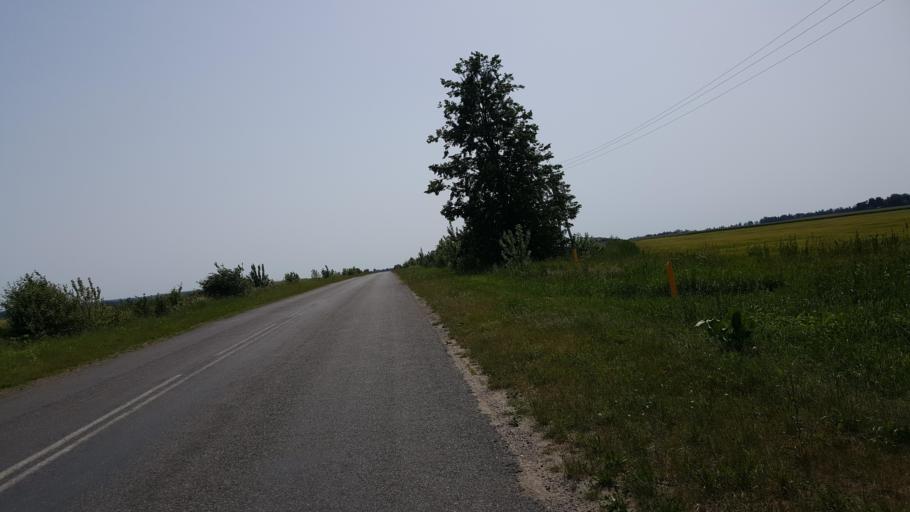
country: BY
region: Brest
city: Kamyanyets
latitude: 52.4206
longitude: 23.8069
